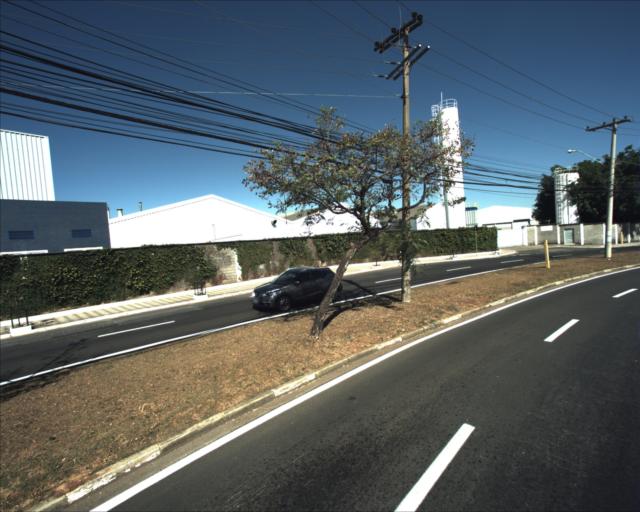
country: BR
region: Sao Paulo
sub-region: Sorocaba
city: Sorocaba
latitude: -23.4780
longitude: -47.4302
